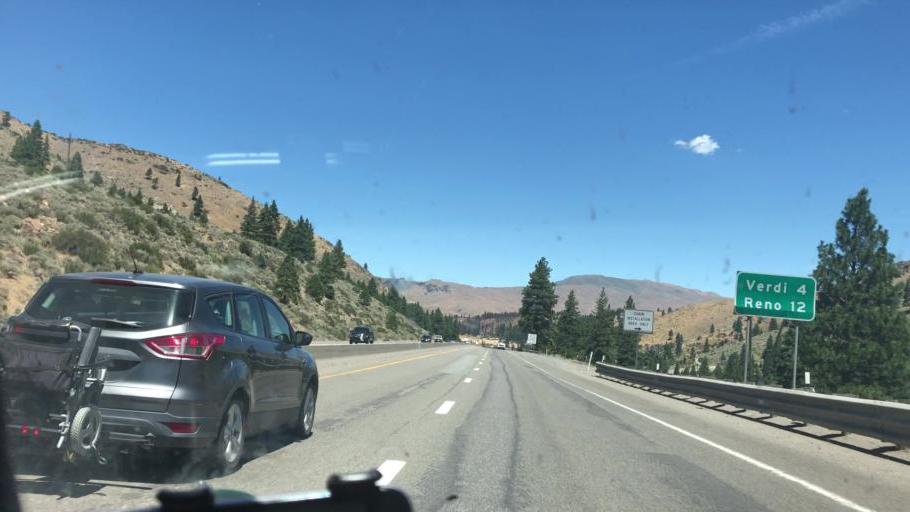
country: US
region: Nevada
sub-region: Washoe County
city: Verdi
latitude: 39.4742
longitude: -119.9968
